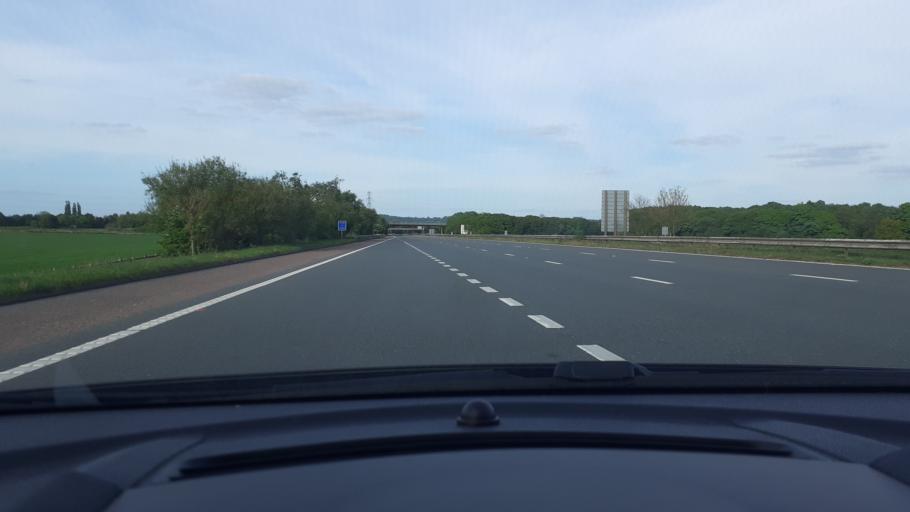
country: GB
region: England
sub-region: Lancashire
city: Skelmersdale
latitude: 53.5387
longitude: -2.8200
